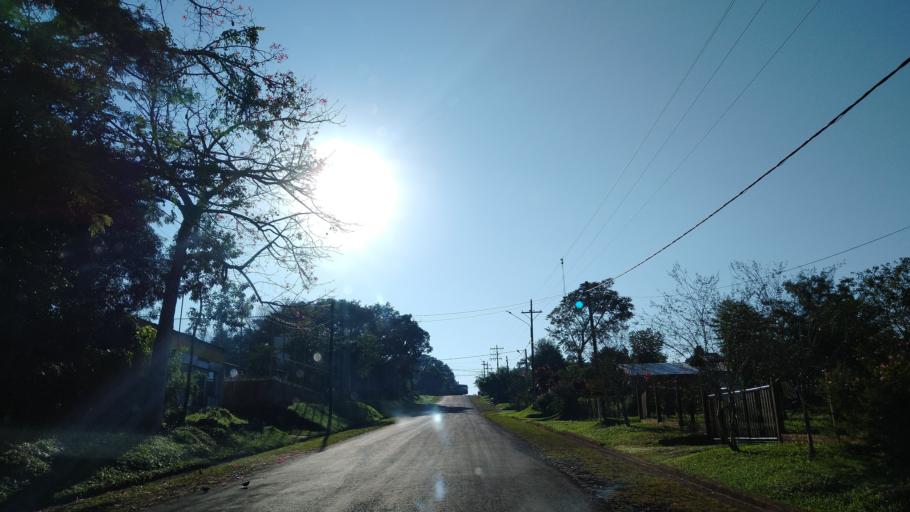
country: AR
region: Misiones
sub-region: Departamento de Montecarlo
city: Montecarlo
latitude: -26.5696
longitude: -54.7687
